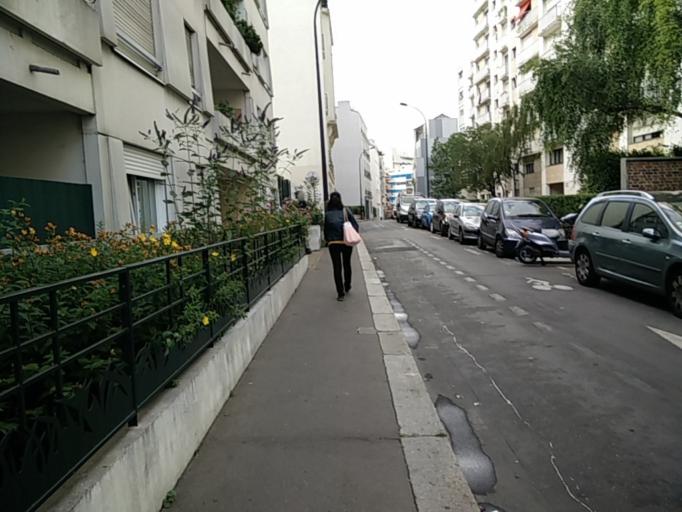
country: FR
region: Ile-de-France
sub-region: Departement de Seine-Saint-Denis
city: Le Pre-Saint-Gervais
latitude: 48.8775
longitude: 2.3894
